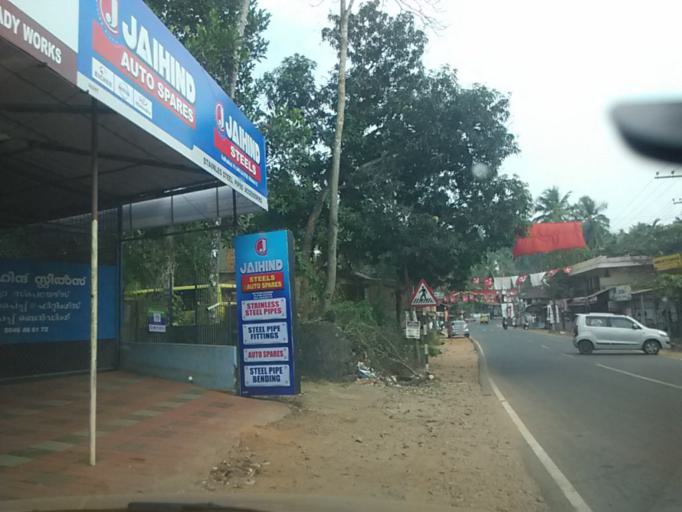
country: IN
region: Kerala
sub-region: Kozhikode
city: Naduvannur
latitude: 11.5446
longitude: 75.7682
